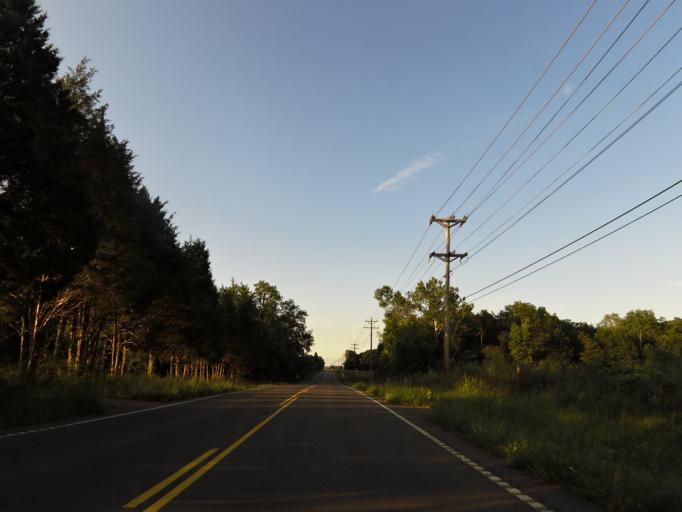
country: US
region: Tennessee
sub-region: Rhea County
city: Spring City
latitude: 35.6677
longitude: -84.6757
